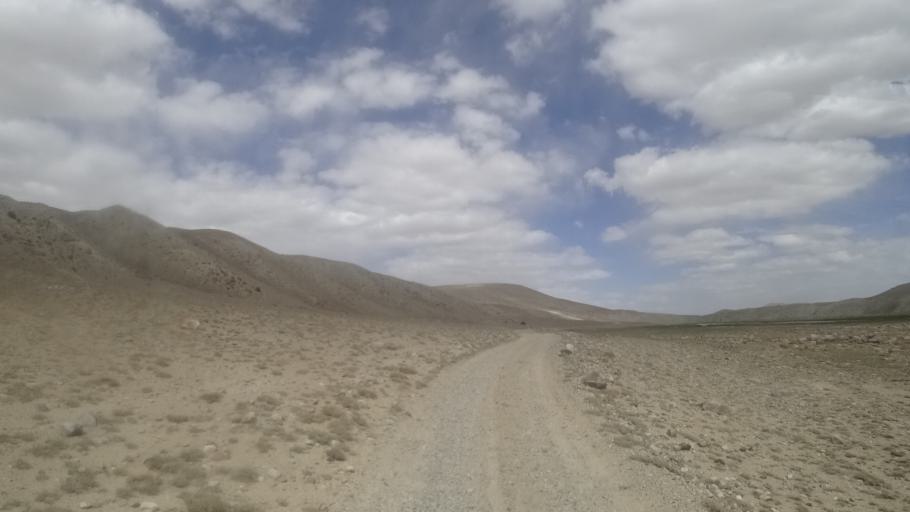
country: AF
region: Badakhshan
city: Khandud
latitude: 37.4071
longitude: 73.1511
